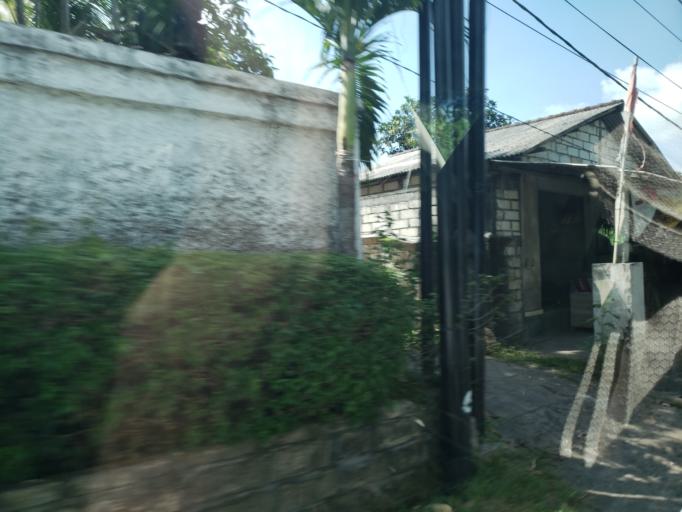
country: ID
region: Bali
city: Kangin
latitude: -8.8223
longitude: 115.1525
